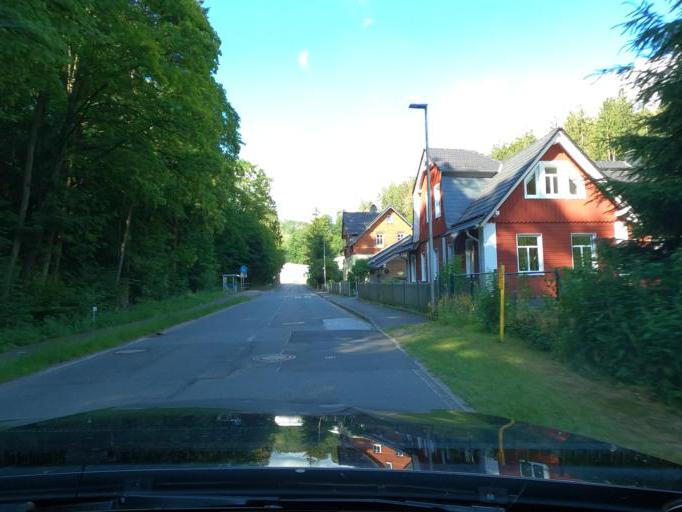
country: DE
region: Lower Saxony
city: Osterode am Harz
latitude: 51.7431
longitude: 10.2849
